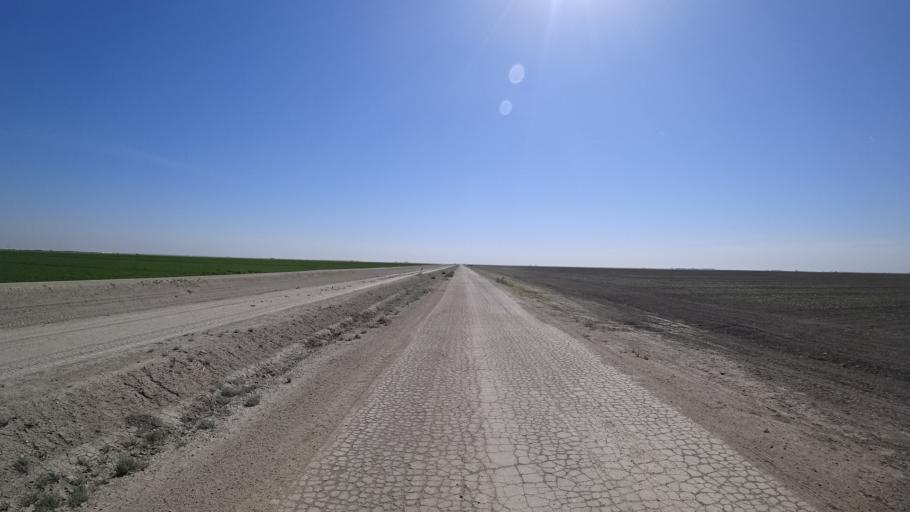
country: US
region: California
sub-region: Kings County
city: Corcoran
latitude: 35.9781
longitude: -119.5688
